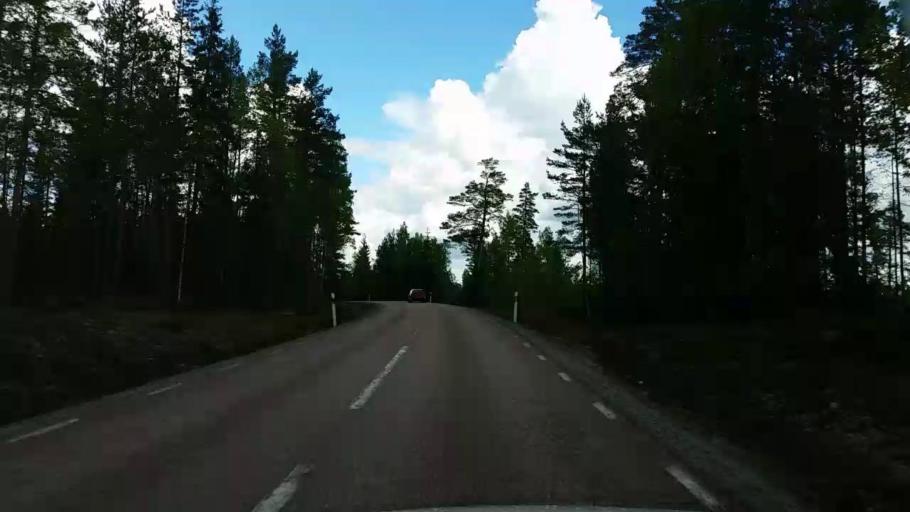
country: SE
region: Vaestmanland
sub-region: Fagersta Kommun
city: Fagersta
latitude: 59.8671
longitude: 15.8422
